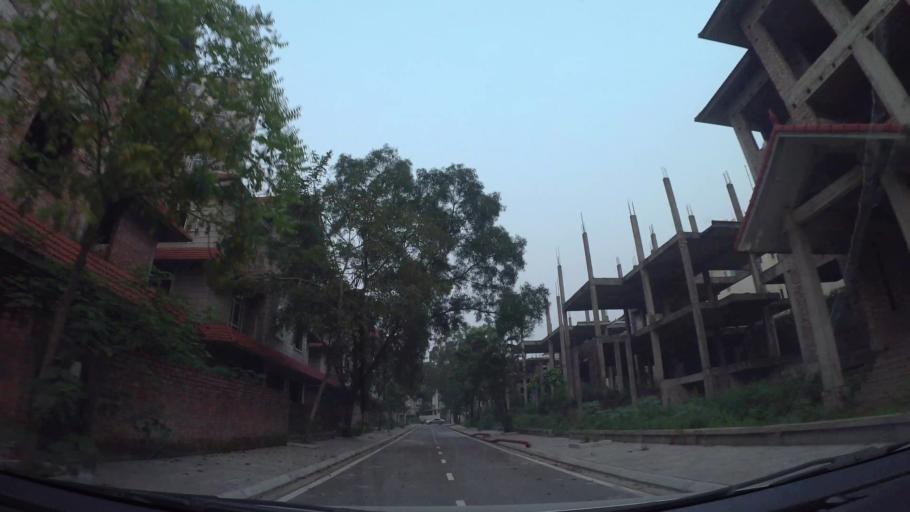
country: VN
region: Ha Noi
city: Cau Dien
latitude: 21.0021
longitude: 105.7313
